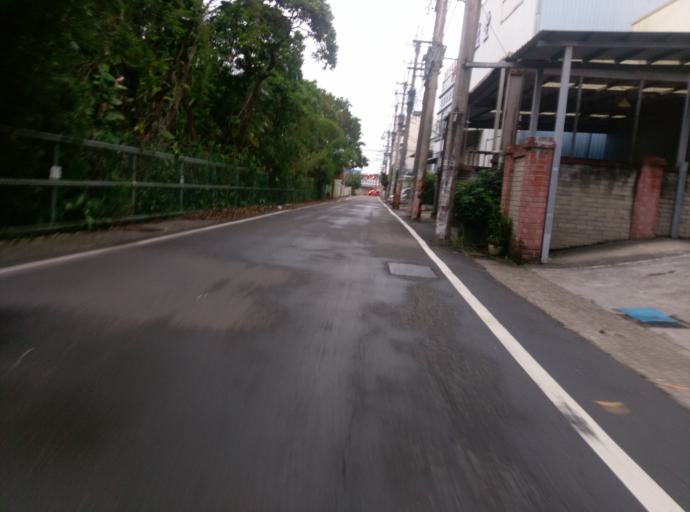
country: TW
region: Taiwan
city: Daxi
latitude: 24.9108
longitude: 121.2400
